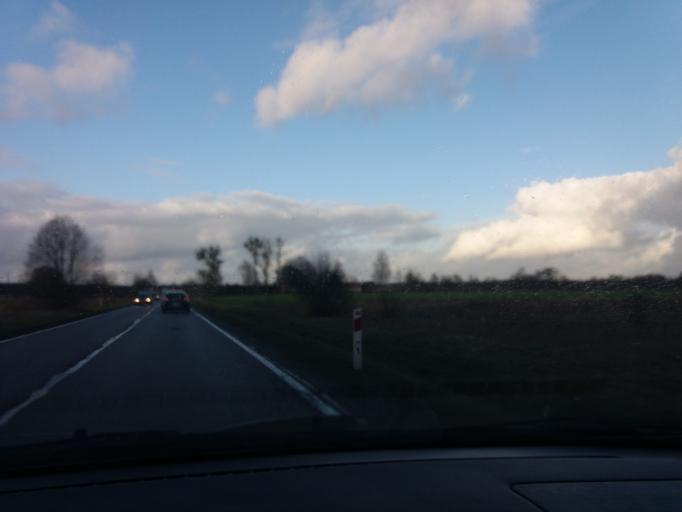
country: PL
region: Warmian-Masurian Voivodeship
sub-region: Powiat szczycienski
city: Wielbark
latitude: 53.4709
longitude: 20.9517
